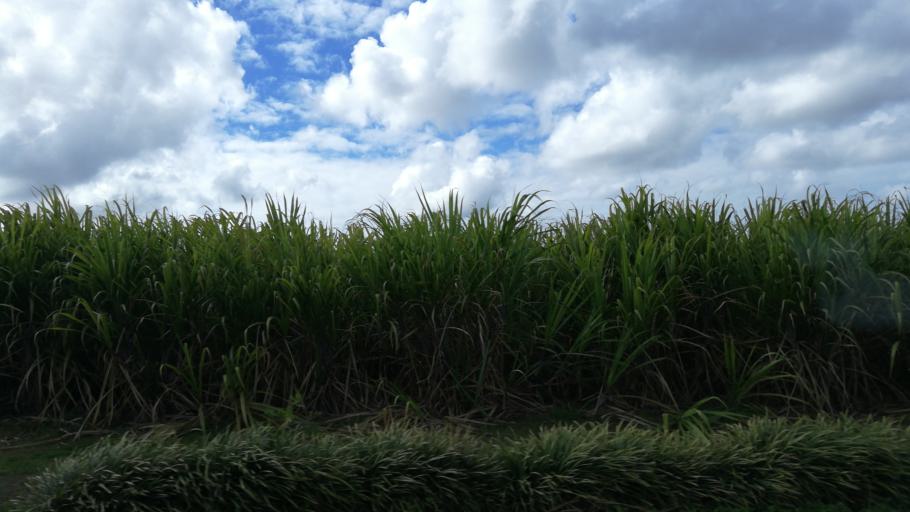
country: MU
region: Flacq
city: Camp de Masque
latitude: -20.2164
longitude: 57.6749
